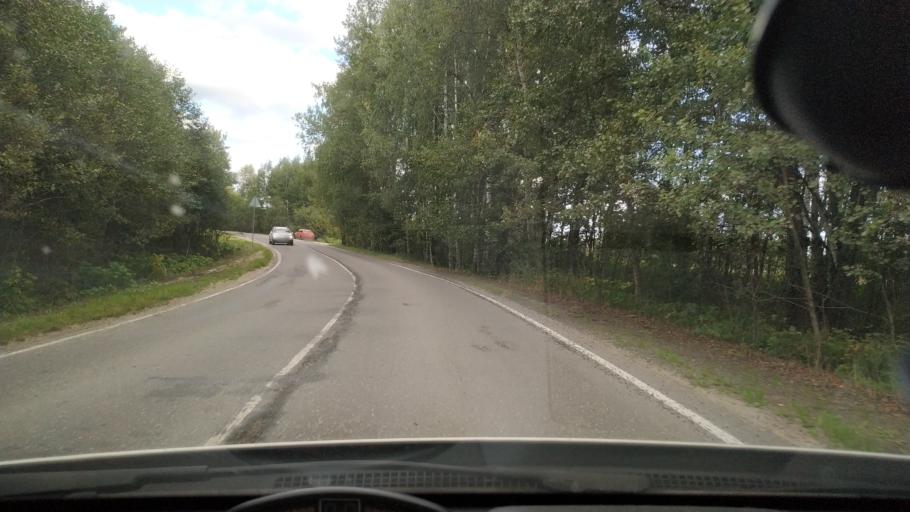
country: RU
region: Moskovskaya
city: Fryazevo
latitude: 55.7210
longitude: 38.4227
